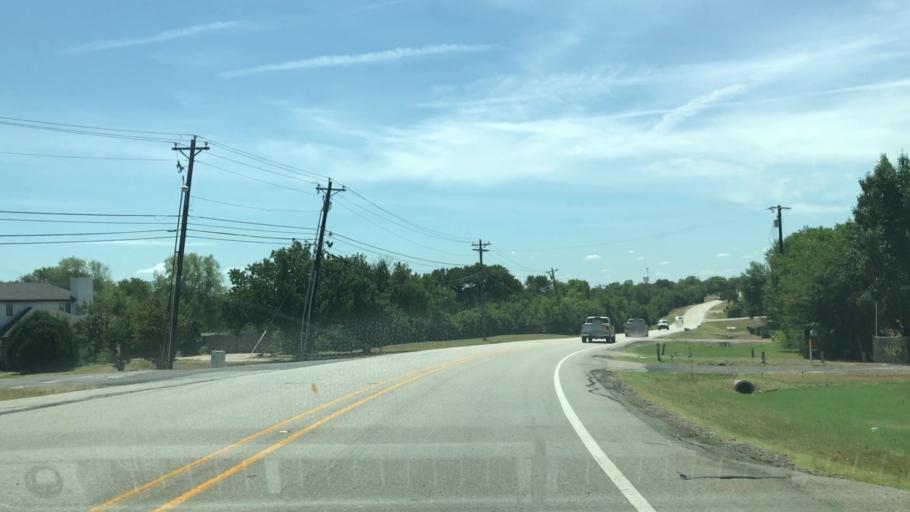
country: US
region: Texas
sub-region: Collin County
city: Saint Paul
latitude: 33.0498
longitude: -96.5496
